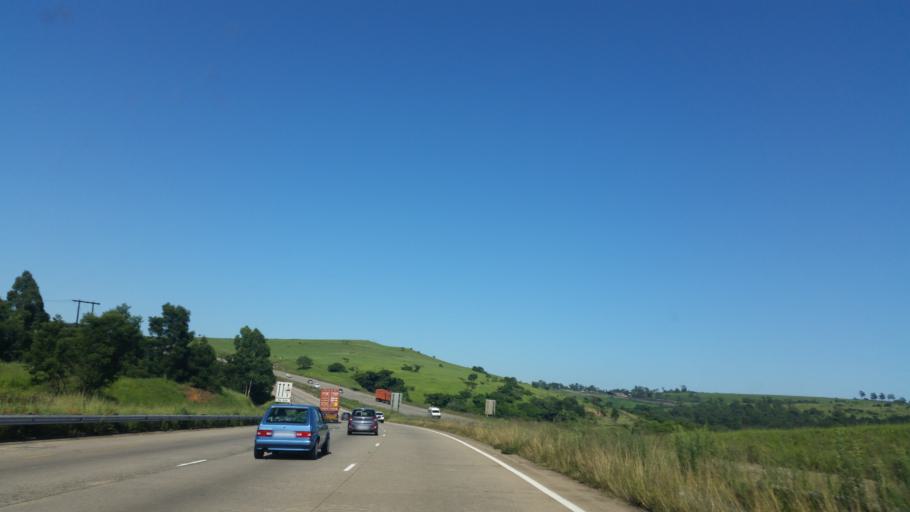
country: ZA
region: KwaZulu-Natal
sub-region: eThekwini Metropolitan Municipality
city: Mpumalanga
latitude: -29.7366
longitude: 30.6464
